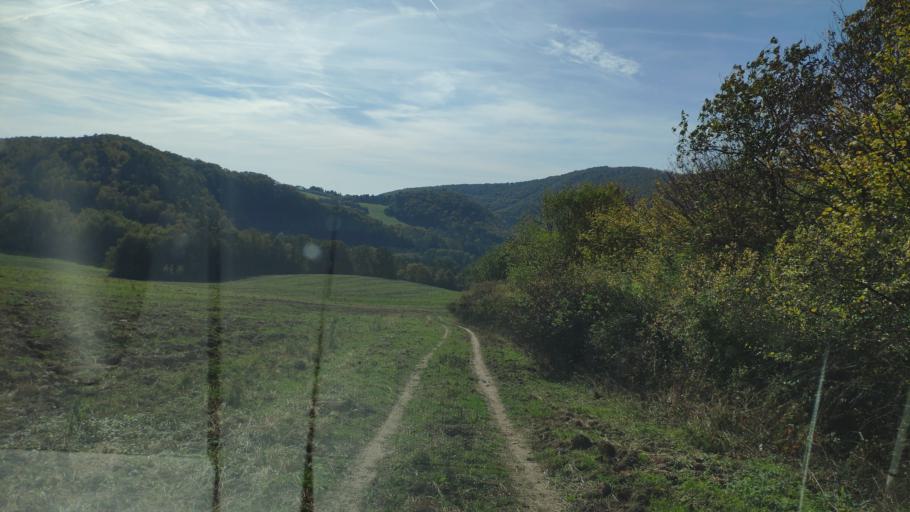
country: SK
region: Presovsky
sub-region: Okres Presov
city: Presov
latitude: 48.8837
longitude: 21.2291
